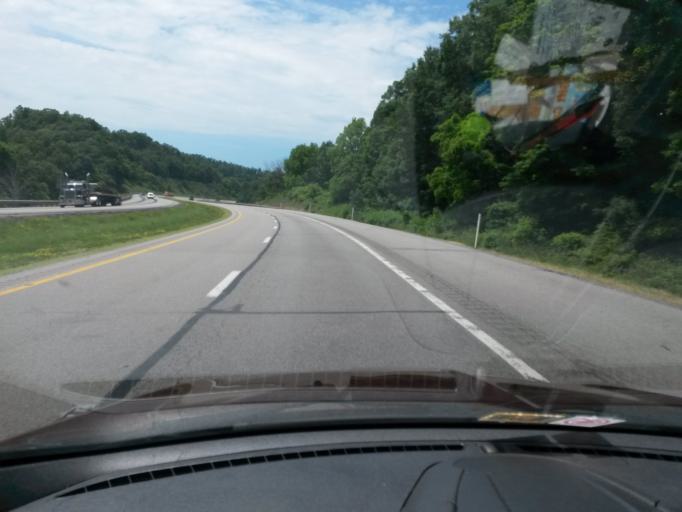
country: US
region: West Virginia
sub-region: Lewis County
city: Weston
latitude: 38.9094
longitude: -80.6027
